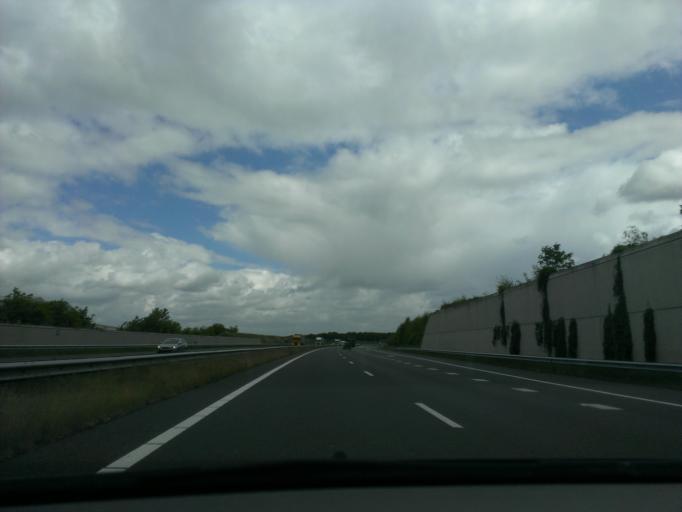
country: NL
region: Limburg
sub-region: Gemeente Beesel
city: Beesel
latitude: 51.2569
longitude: 6.0592
